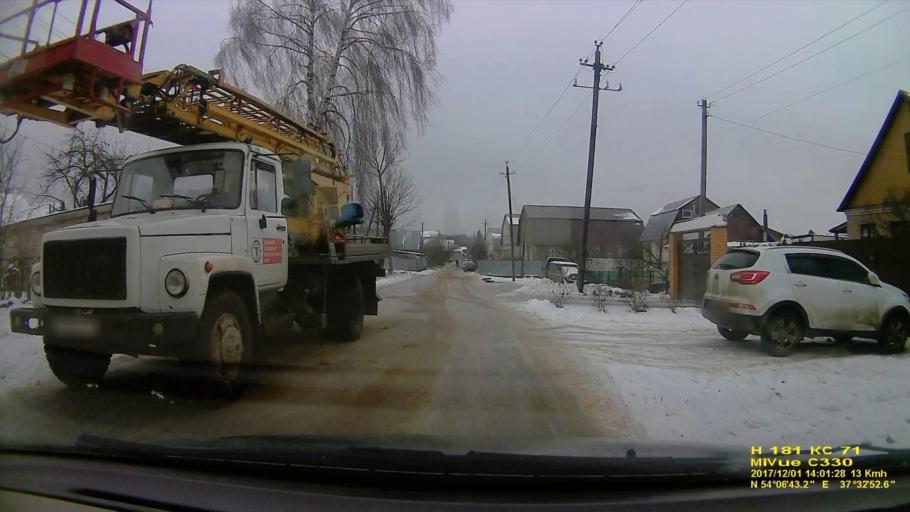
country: RU
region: Tula
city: Kosaya Gora
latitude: 54.1120
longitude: 37.5480
